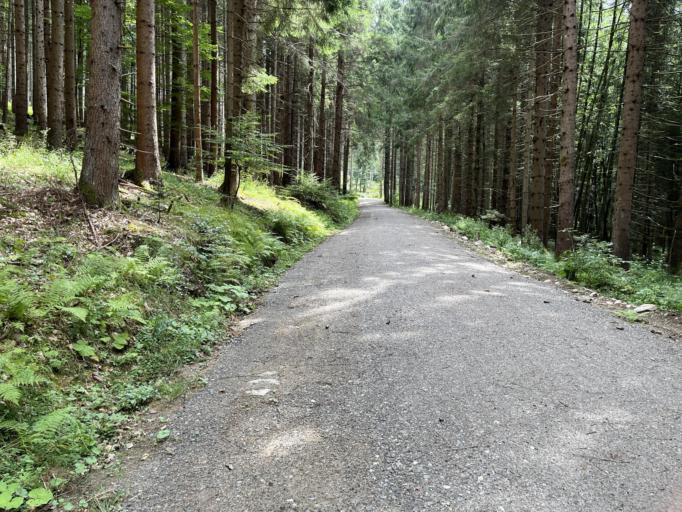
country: AT
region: Carinthia
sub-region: Politischer Bezirk Spittal an der Drau
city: Millstatt
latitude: 46.7942
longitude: 13.5474
